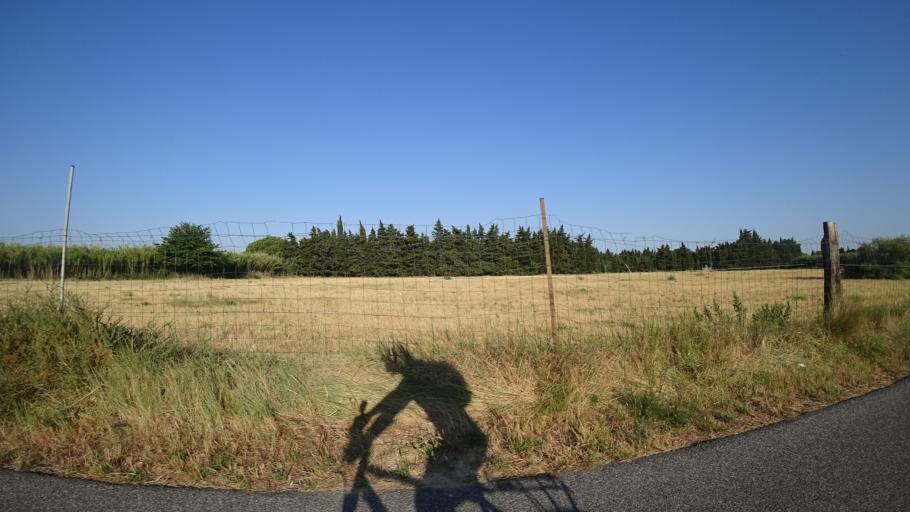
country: FR
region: Languedoc-Roussillon
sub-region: Departement des Pyrenees-Orientales
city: Sainte-Marie-Plage
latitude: 42.7239
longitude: 3.0296
